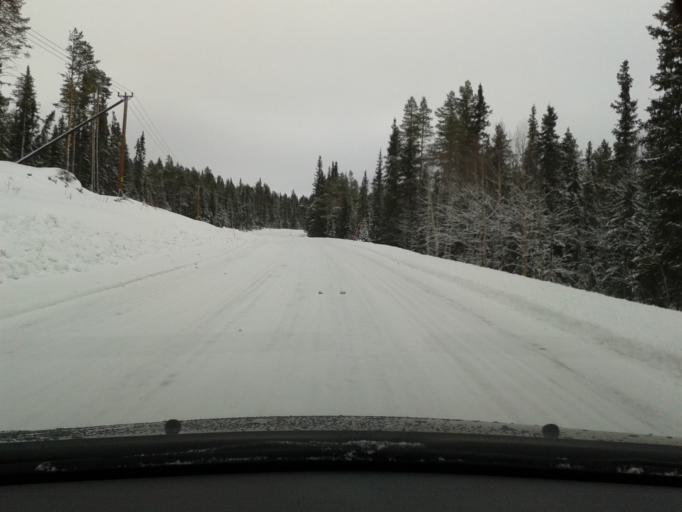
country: SE
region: Vaesterbotten
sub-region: Vilhelmina Kommun
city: Sjoberg
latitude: 65.2283
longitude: 15.9101
